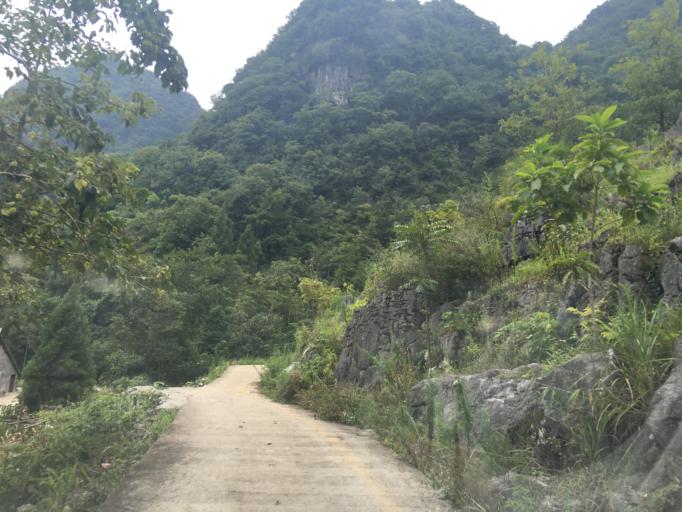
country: CN
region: Guangxi Zhuangzu Zizhiqu
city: Xinzhou
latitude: 25.2262
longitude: 105.6370
